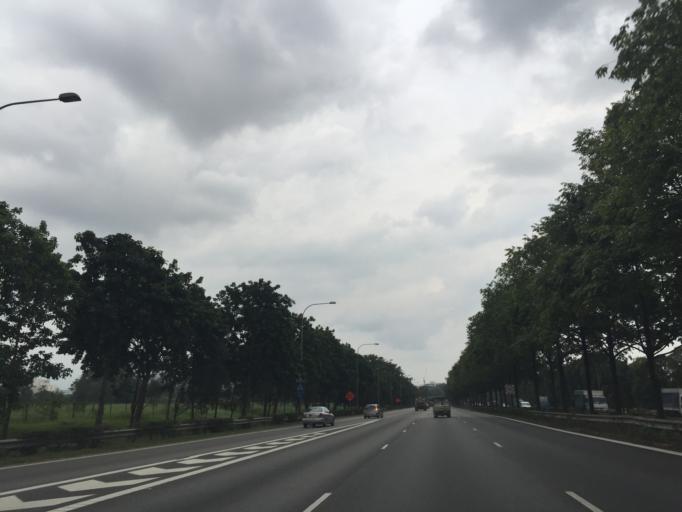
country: SG
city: Singapore
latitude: 1.3258
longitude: 103.7288
